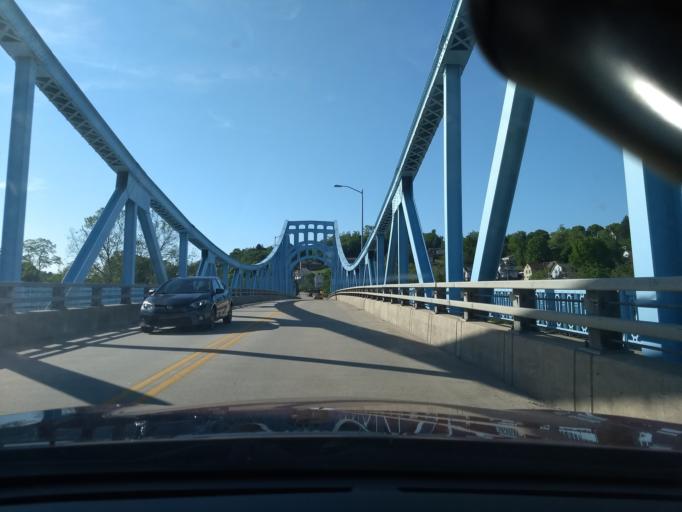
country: US
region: Pennsylvania
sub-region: Allegheny County
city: Versailles
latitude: 40.3126
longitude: -79.8280
